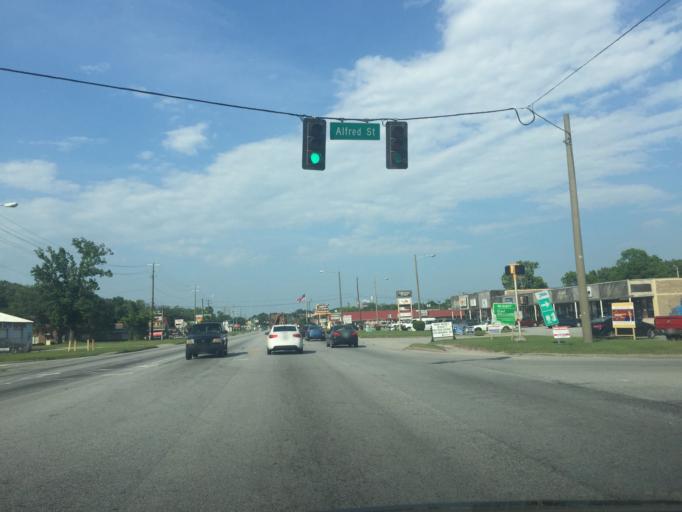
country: US
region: Georgia
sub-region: Chatham County
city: Garden City
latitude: 32.0928
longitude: -81.1495
